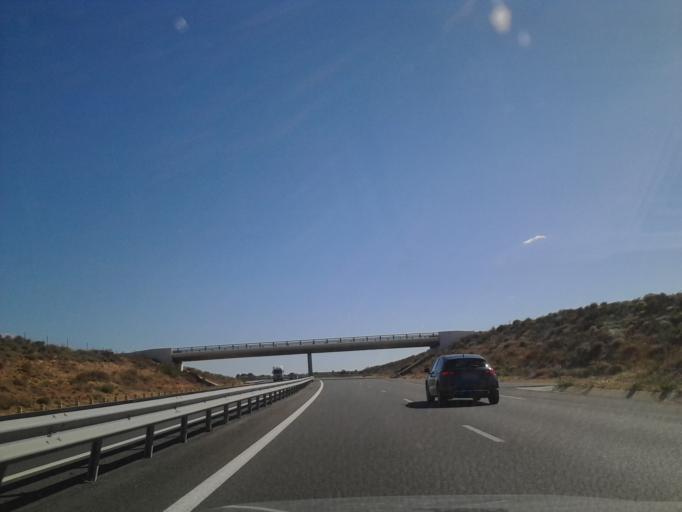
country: FR
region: Languedoc-Roussillon
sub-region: Departement de l'Herault
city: Valros
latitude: 43.4144
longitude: 3.3799
